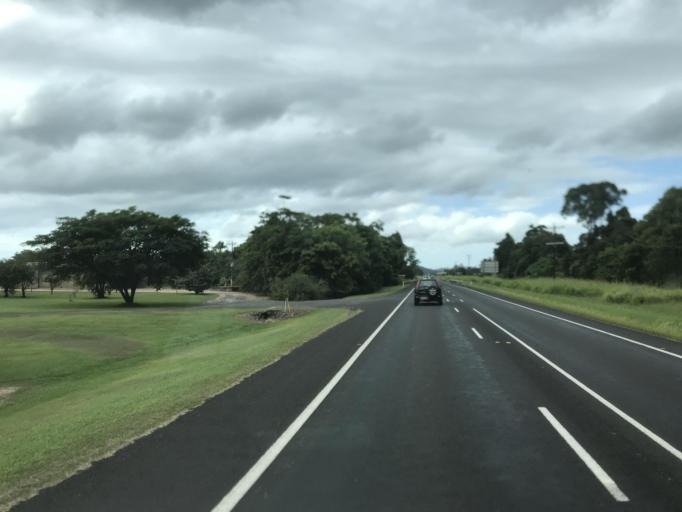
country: AU
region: Queensland
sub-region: Cassowary Coast
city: Innisfail
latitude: -17.7520
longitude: 146.0277
